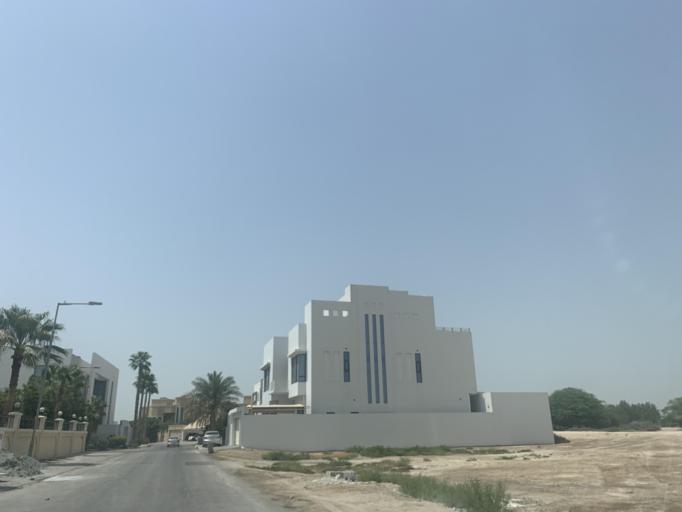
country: BH
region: Manama
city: Jidd Hafs
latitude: 26.1994
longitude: 50.5053
